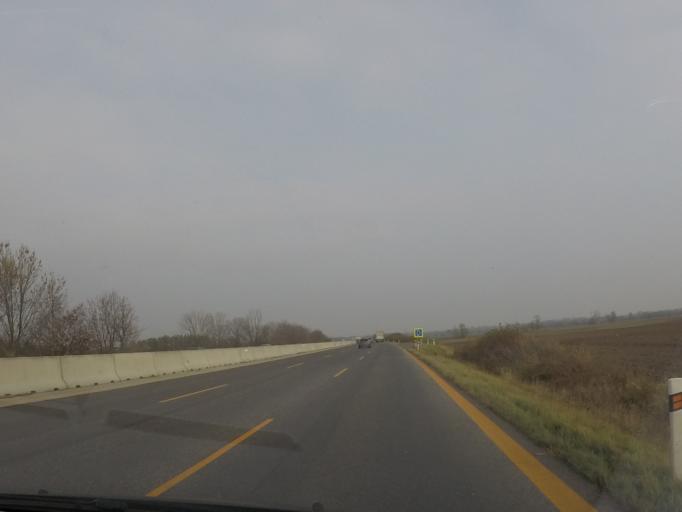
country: SK
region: Bratislavsky
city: Senec
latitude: 48.2552
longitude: 17.4402
